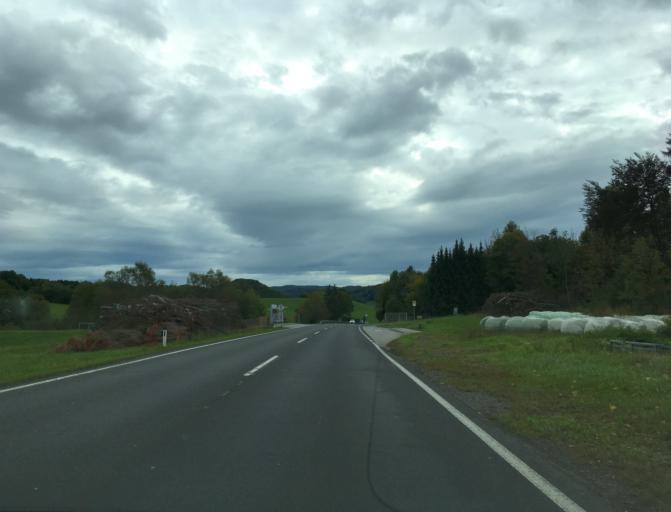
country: AT
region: Lower Austria
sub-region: Politischer Bezirk Wiener Neustadt
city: Bad Schonau
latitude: 47.5125
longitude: 16.2004
